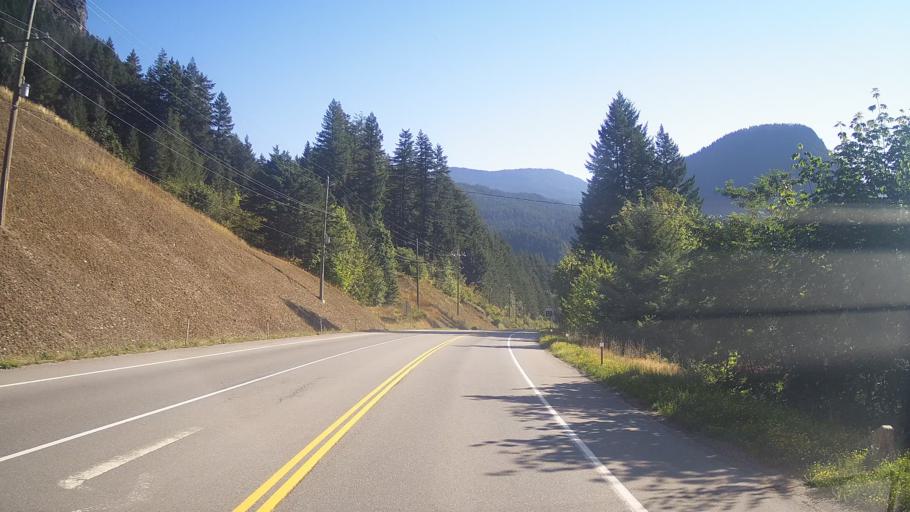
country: CA
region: British Columbia
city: Hope
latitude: 49.5595
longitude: -121.4423
